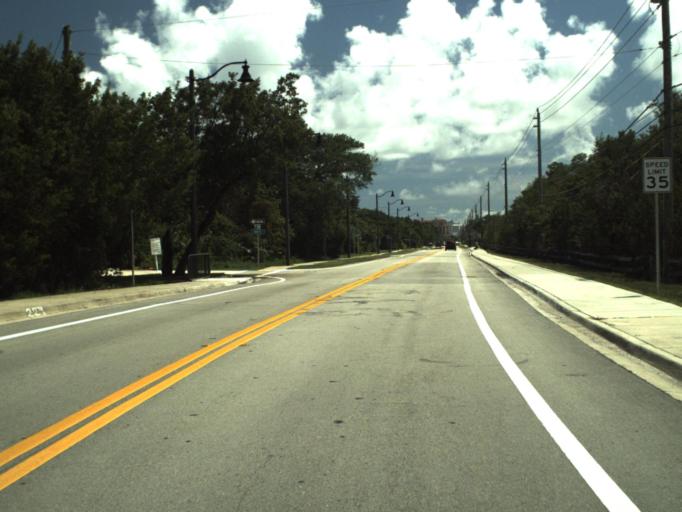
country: US
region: Florida
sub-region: Broward County
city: Dania Beach
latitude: 26.0477
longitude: -80.1146
